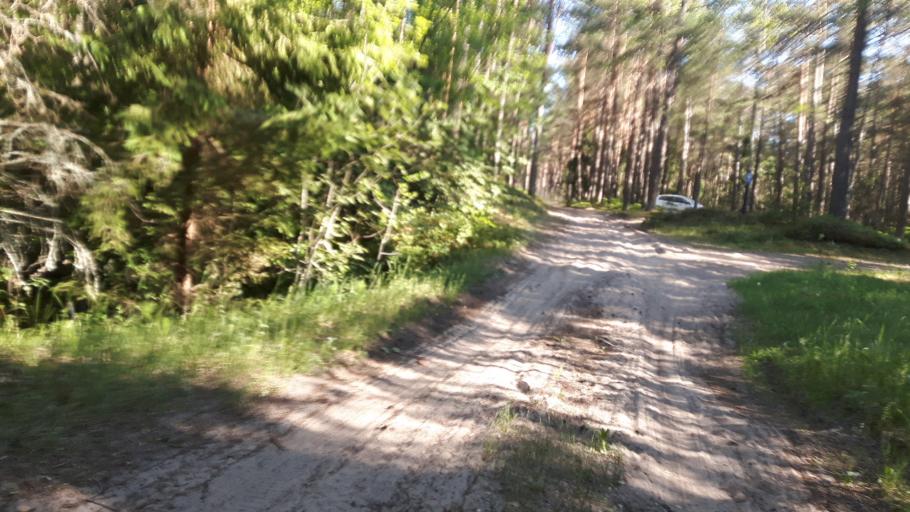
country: LV
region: Salacgrivas
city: Salacgriva
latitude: 57.7102
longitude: 24.3519
